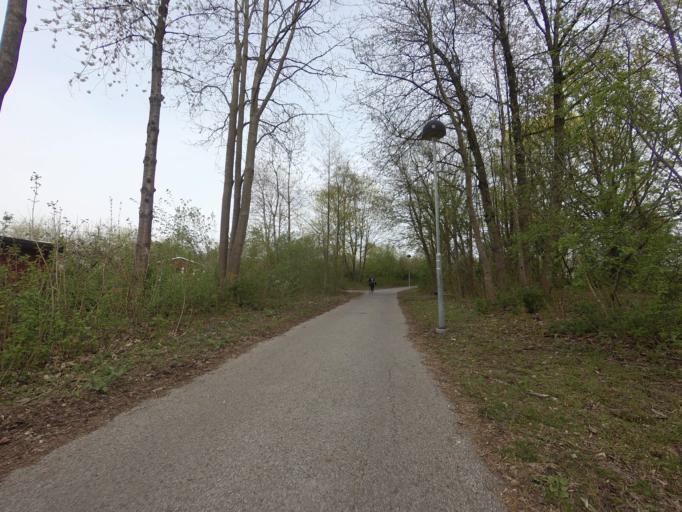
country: SE
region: Skane
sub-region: Lunds Kommun
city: Lund
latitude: 55.7216
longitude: 13.1723
